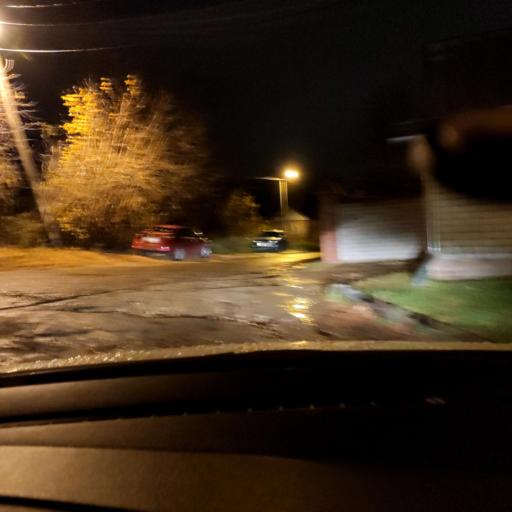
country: RU
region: Tatarstan
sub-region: Gorod Kazan'
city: Kazan
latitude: 55.8369
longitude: 49.2083
